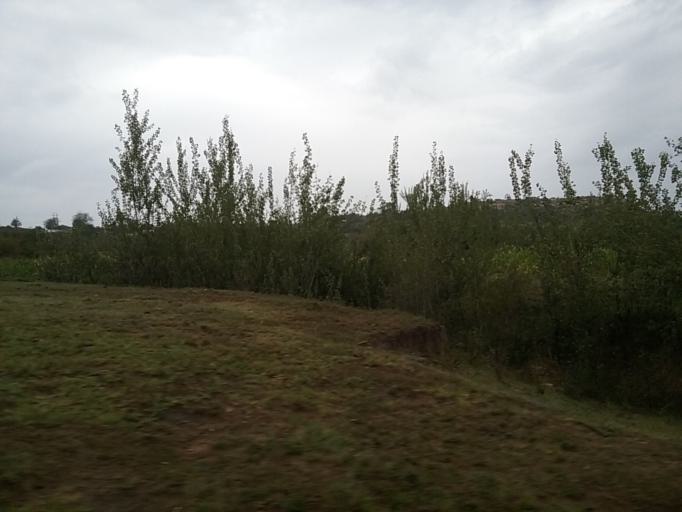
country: LS
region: Berea
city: Teyateyaneng
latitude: -29.1281
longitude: 27.7382
